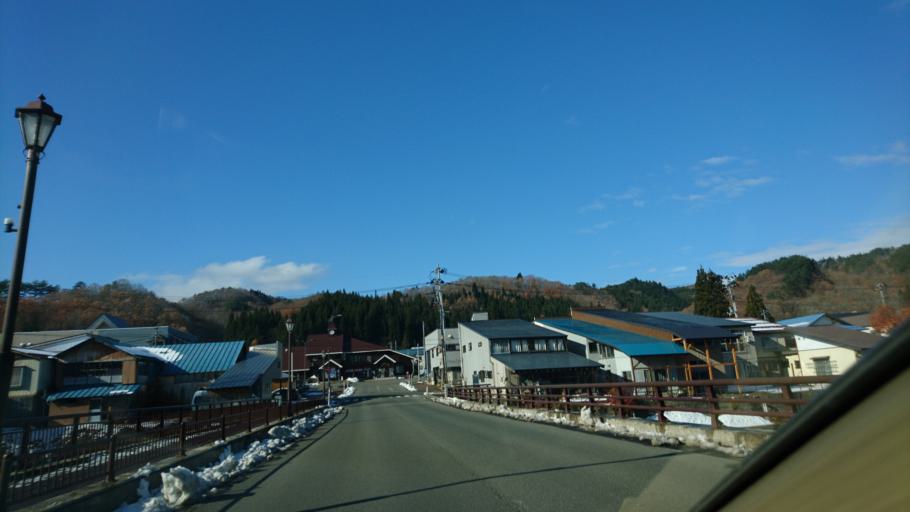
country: JP
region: Akita
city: Yokotemachi
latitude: 39.3139
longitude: 140.7772
